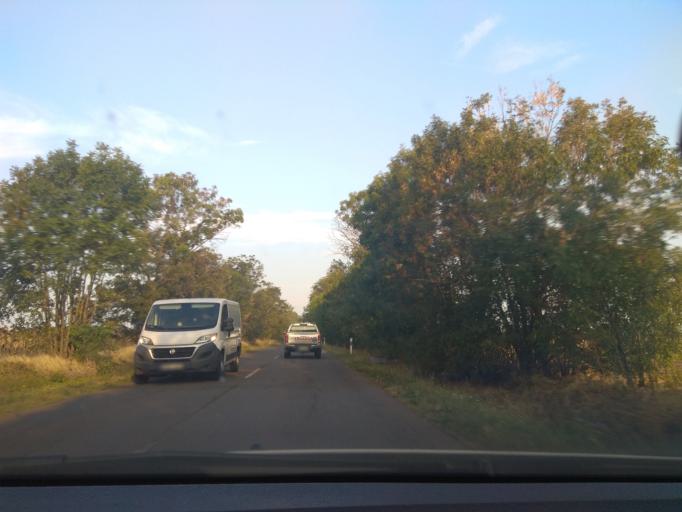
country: HU
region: Heves
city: Ostoros
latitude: 47.8288
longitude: 20.4589
